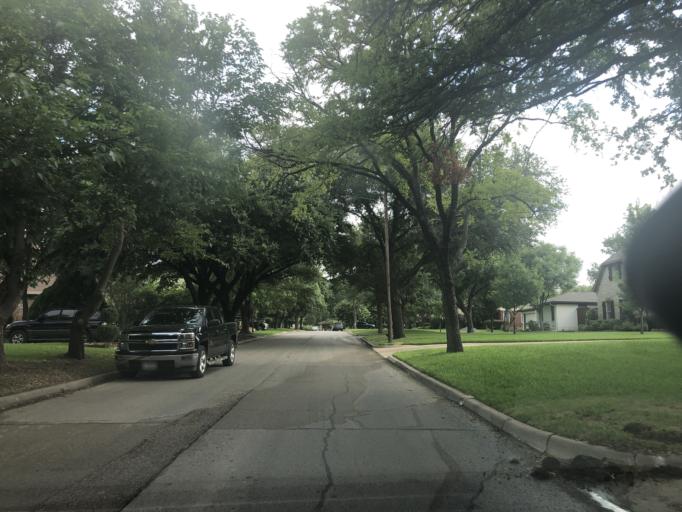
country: US
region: Texas
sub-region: Dallas County
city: University Park
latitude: 32.8643
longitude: -96.8468
